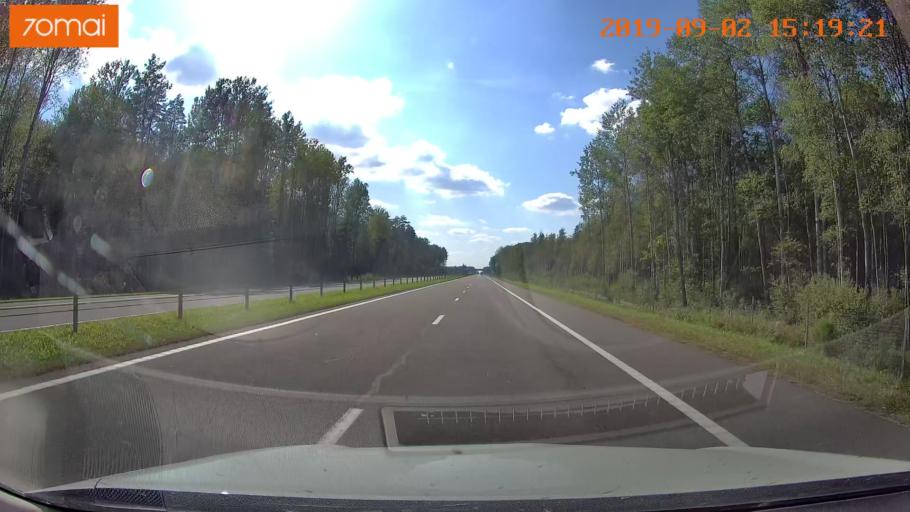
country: BY
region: Mogilev
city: Byalynichy
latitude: 53.9346
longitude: 29.5399
